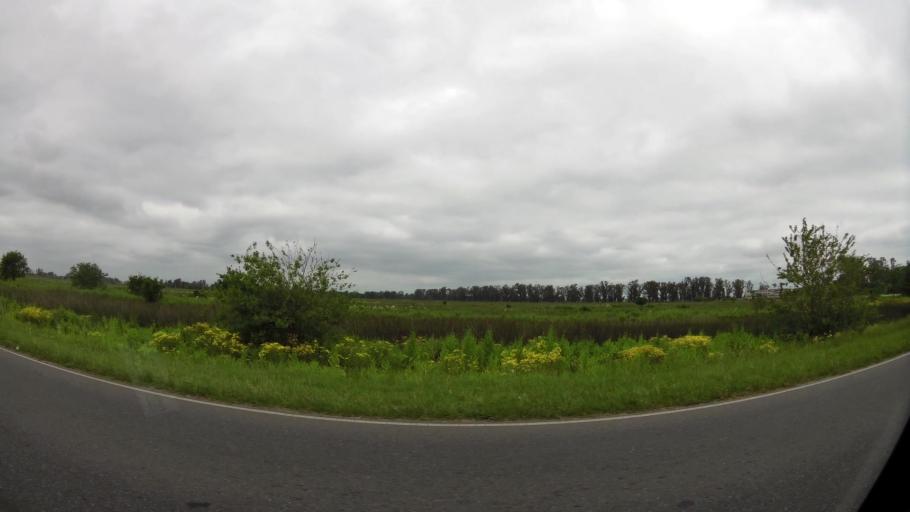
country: AR
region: Buenos Aires
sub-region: Partido de San Vicente
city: San Vicente
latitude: -34.9879
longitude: -58.4682
